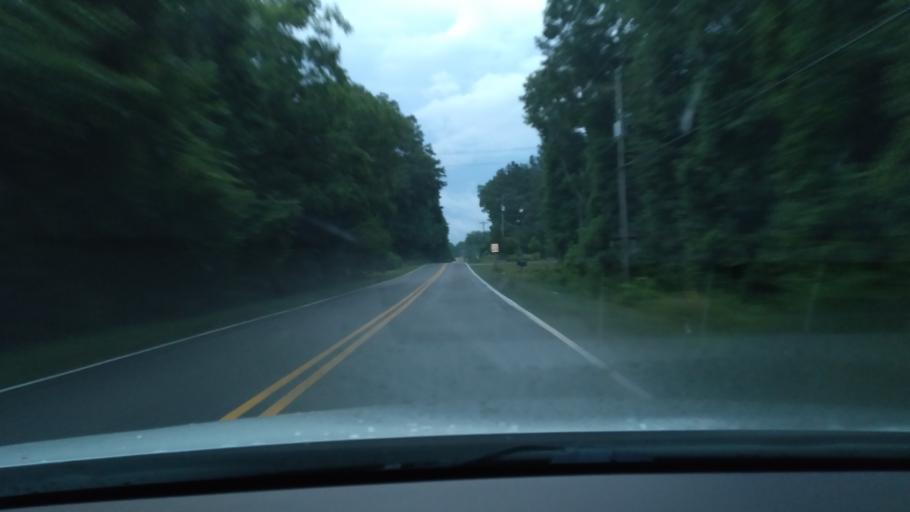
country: US
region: North Carolina
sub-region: Guilford County
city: McLeansville
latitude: 36.0617
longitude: -79.7057
